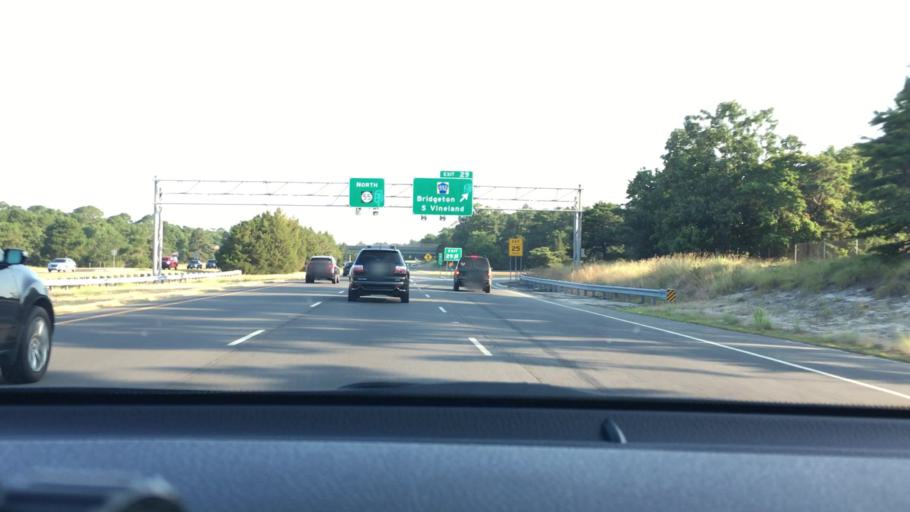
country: US
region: New Jersey
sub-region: Cumberland County
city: South Vineland
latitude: 39.4447
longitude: -75.0624
